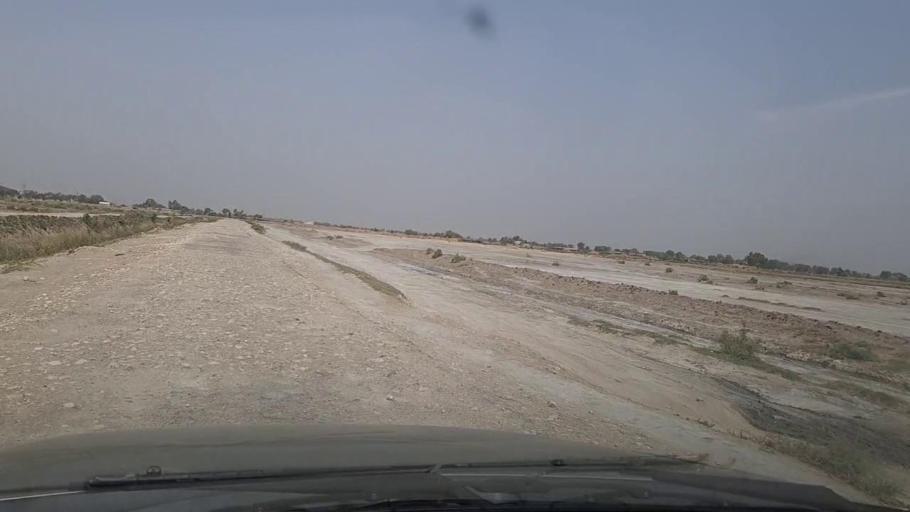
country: PK
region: Balochistan
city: Sohbatpur
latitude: 28.4128
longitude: 68.6937
